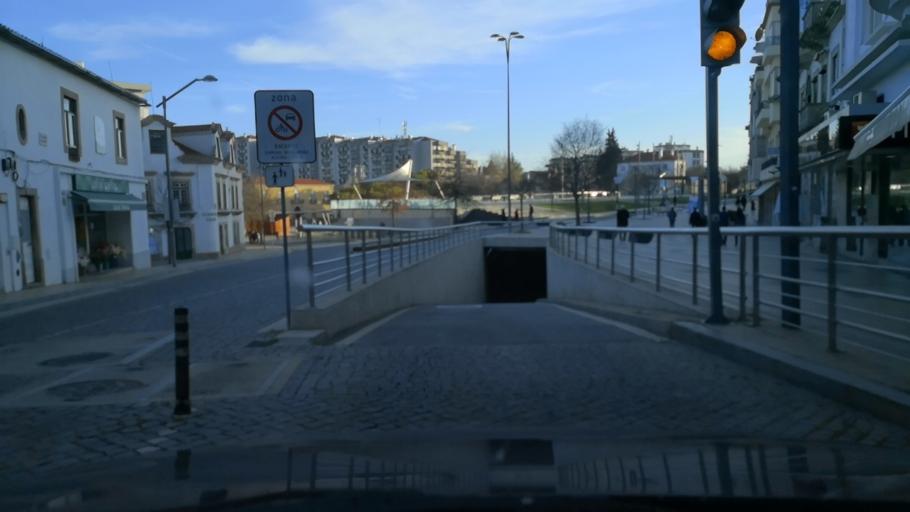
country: PT
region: Castelo Branco
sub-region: Castelo Branco
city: Castelo Branco
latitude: 39.8250
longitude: -7.4912
